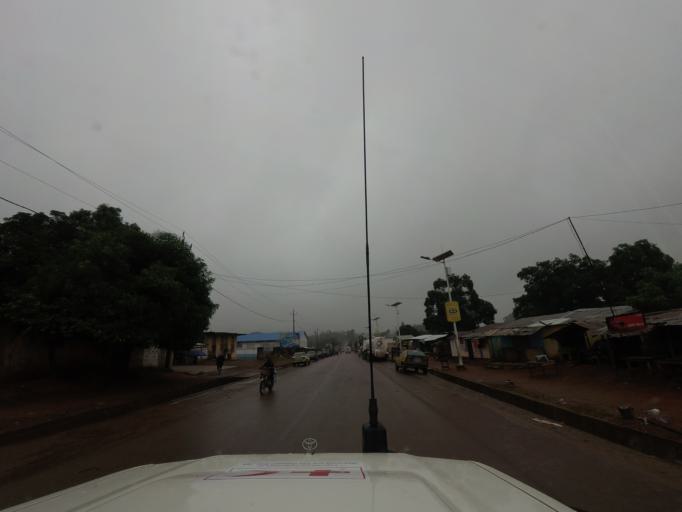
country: GN
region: Nzerekore
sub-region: Nzerekore Prefecture
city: Nzerekore
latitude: 7.7388
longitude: -8.8263
